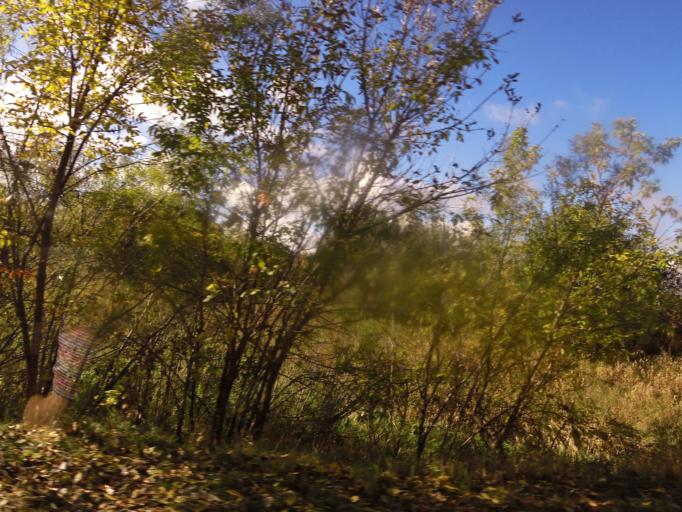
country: US
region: Minnesota
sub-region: Dakota County
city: Eagan
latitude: 44.8232
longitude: -93.2229
